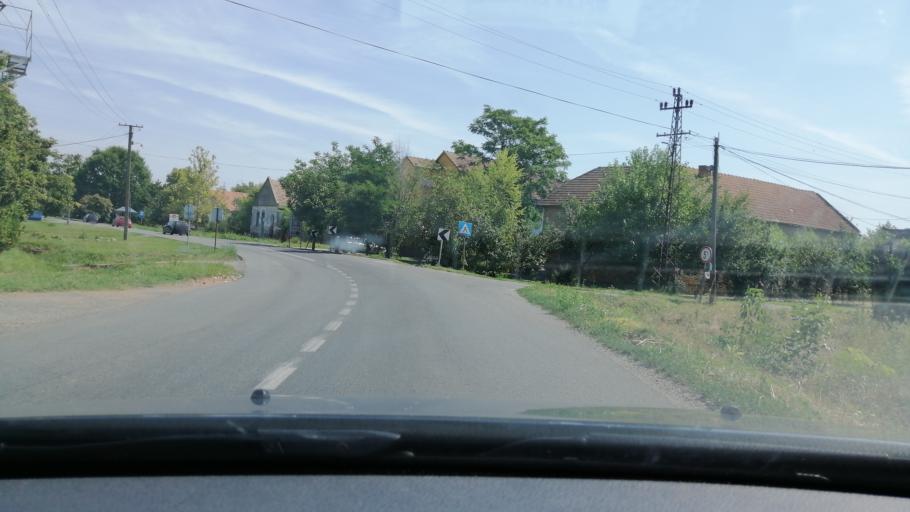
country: RS
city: Lazarevo
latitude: 45.3863
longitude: 20.5294
